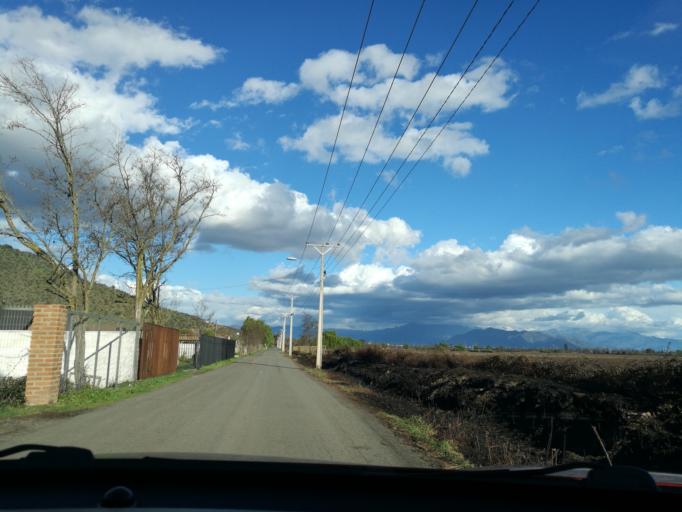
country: CL
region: O'Higgins
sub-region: Provincia de Cachapoal
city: Graneros
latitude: -34.0947
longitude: -70.8198
